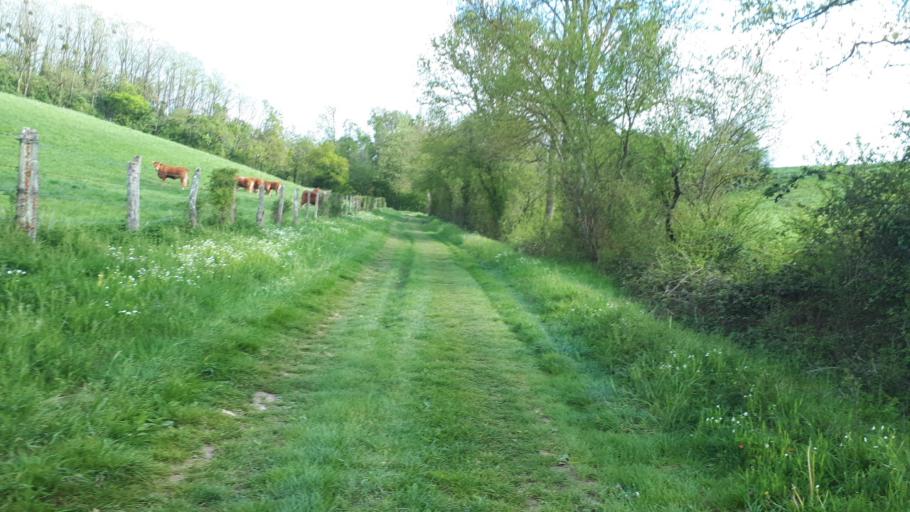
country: FR
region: Centre
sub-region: Departement du Loir-et-Cher
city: Aze
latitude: 47.8393
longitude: 0.9973
